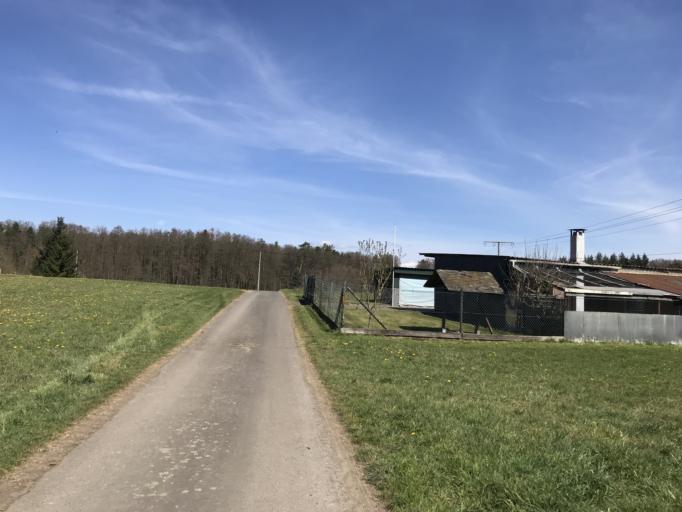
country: DE
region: Hesse
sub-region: Regierungsbezirk Giessen
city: Alten Buseck
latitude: 50.6424
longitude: 8.7445
